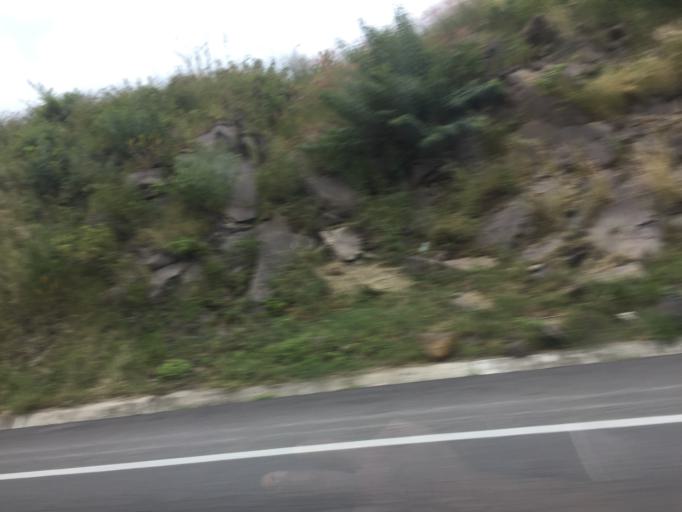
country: MX
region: Jalisco
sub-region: Zapotlanejo
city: La Mezquitera
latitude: 20.5560
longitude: -103.0625
